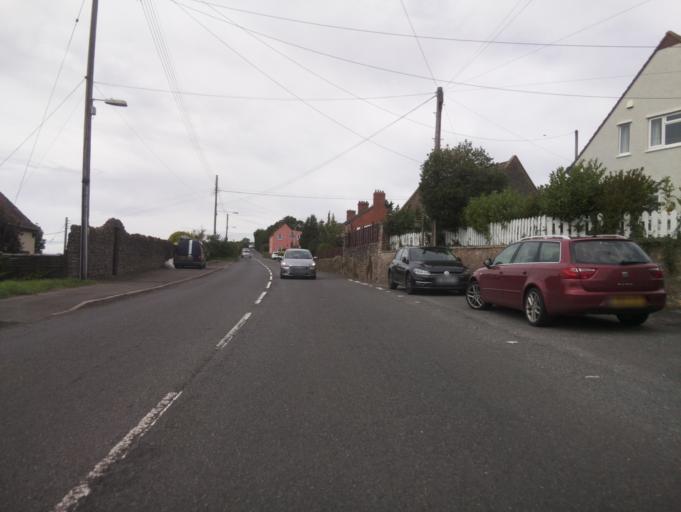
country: GB
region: England
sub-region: Somerset
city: Wells
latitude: 51.2280
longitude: -2.7019
